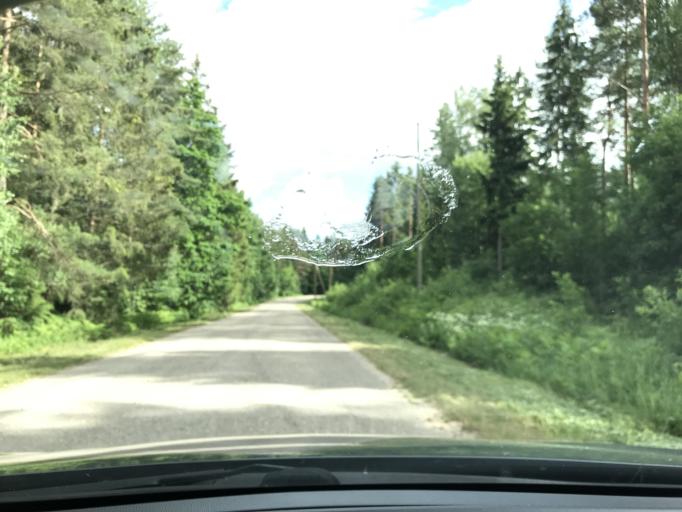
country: LV
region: Alsunga
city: Alsunga
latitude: 56.9876
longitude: 21.6294
